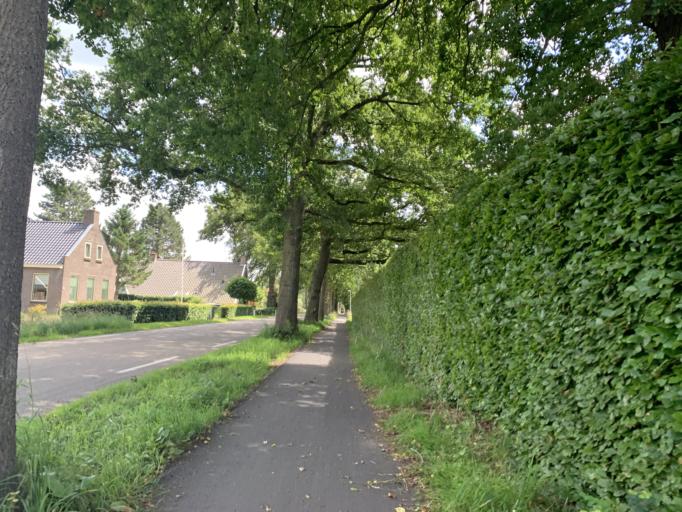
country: NL
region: Groningen
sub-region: Gemeente Haren
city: Haren
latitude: 53.1540
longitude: 6.6433
